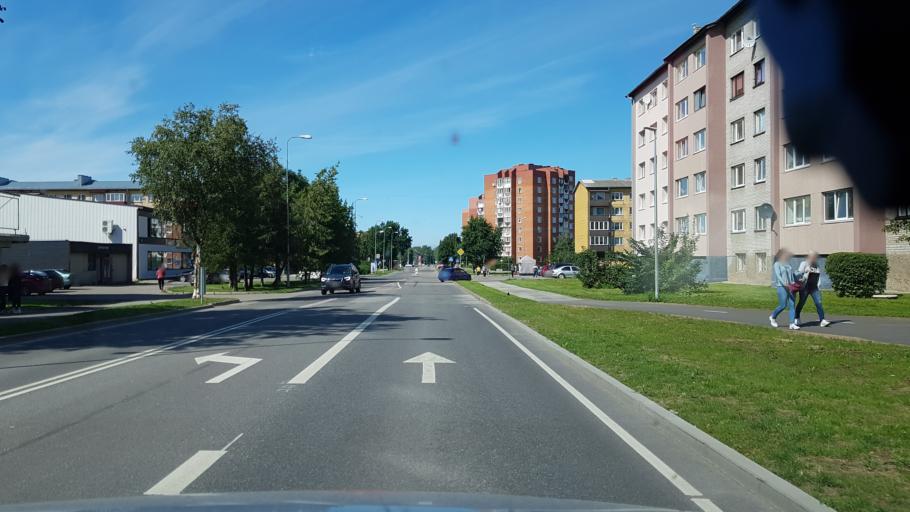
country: EE
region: Ida-Virumaa
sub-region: Kohtla-Jaerve linn
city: Kohtla-Jarve
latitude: 59.4047
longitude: 27.2847
